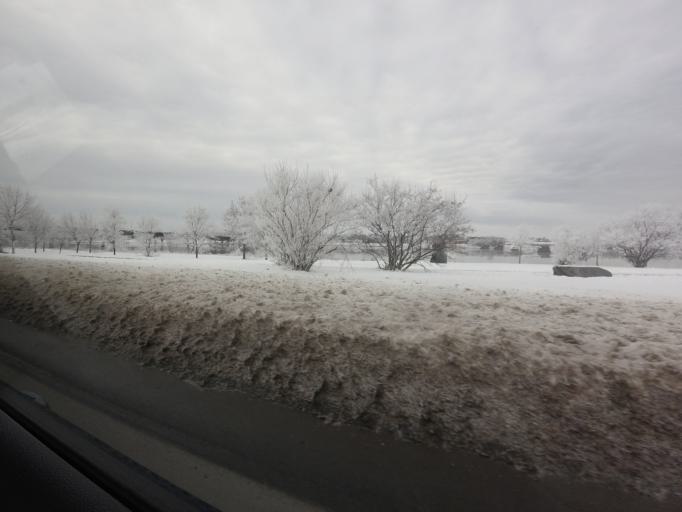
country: CA
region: New Brunswick
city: Fredericton
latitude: 45.9645
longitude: -66.6419
